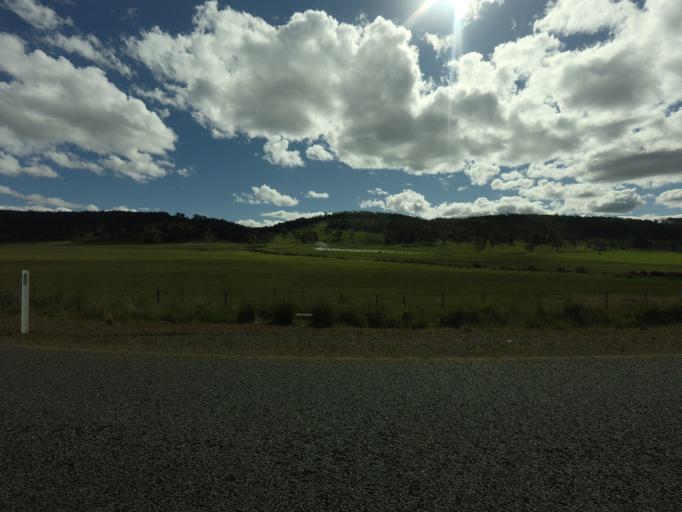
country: AU
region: Tasmania
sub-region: Brighton
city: Bridgewater
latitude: -42.4268
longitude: 147.3122
